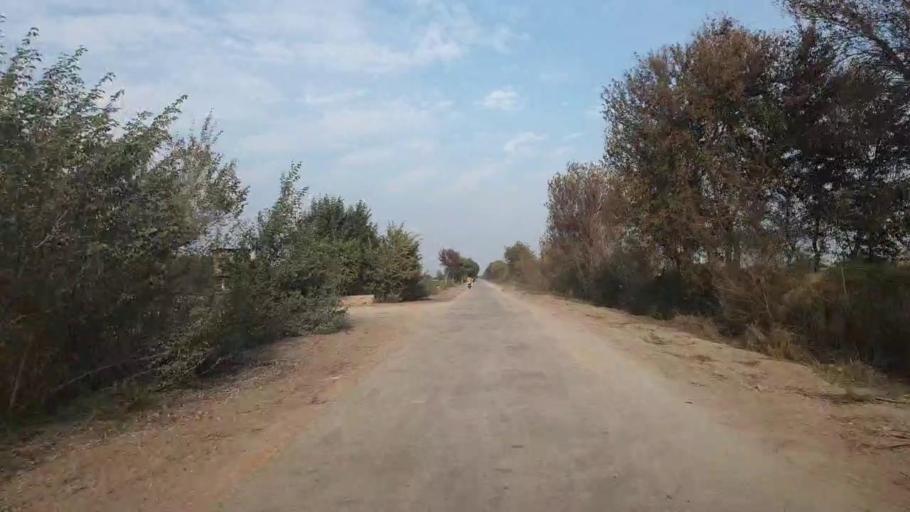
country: PK
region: Sindh
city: Shahdadpur
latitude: 26.0388
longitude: 68.5539
